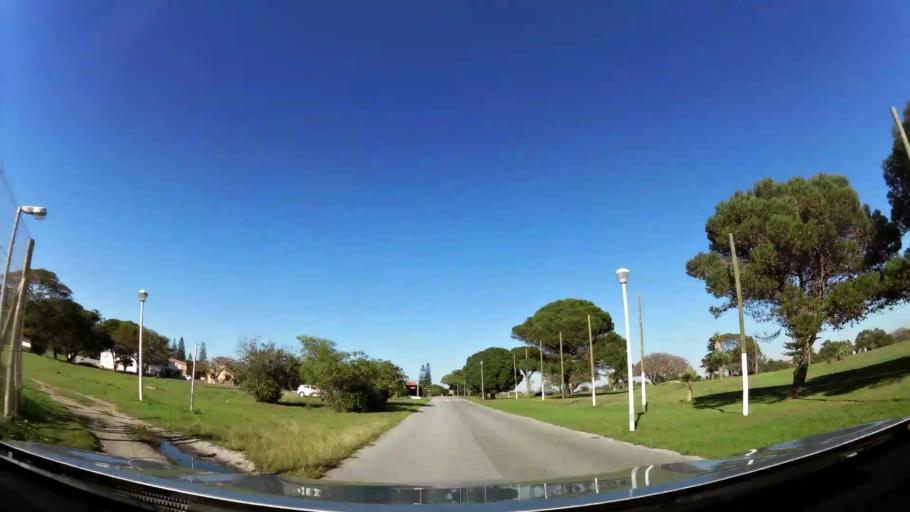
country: ZA
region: Eastern Cape
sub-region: Nelson Mandela Bay Metropolitan Municipality
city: Port Elizabeth
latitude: -33.9843
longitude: 25.6255
